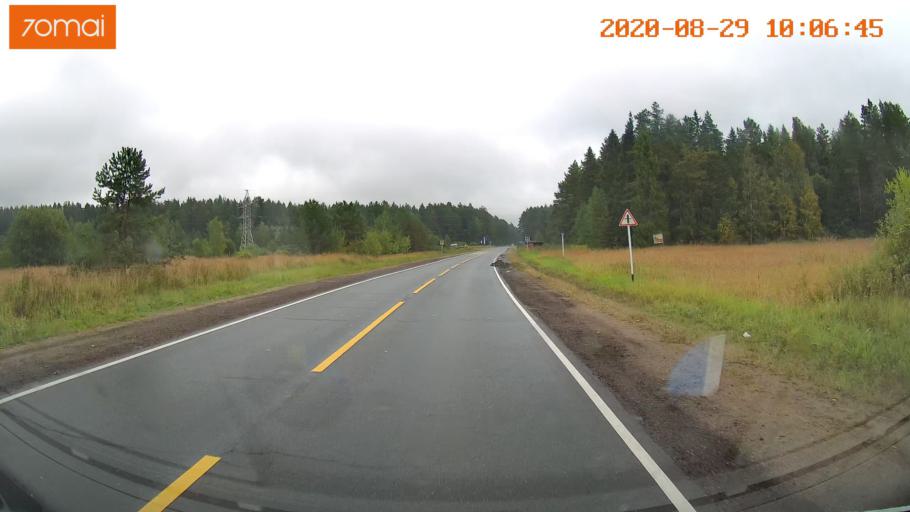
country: RU
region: Ivanovo
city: Kuznechikha
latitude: 57.3867
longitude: 42.5527
